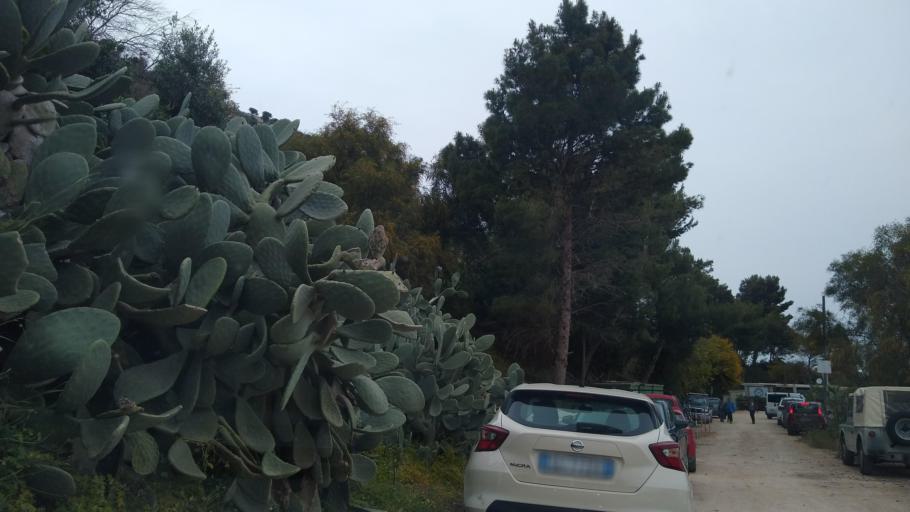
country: IT
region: Sicily
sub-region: Trapani
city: Castellammare del Golfo
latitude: 38.0288
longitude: 12.8785
